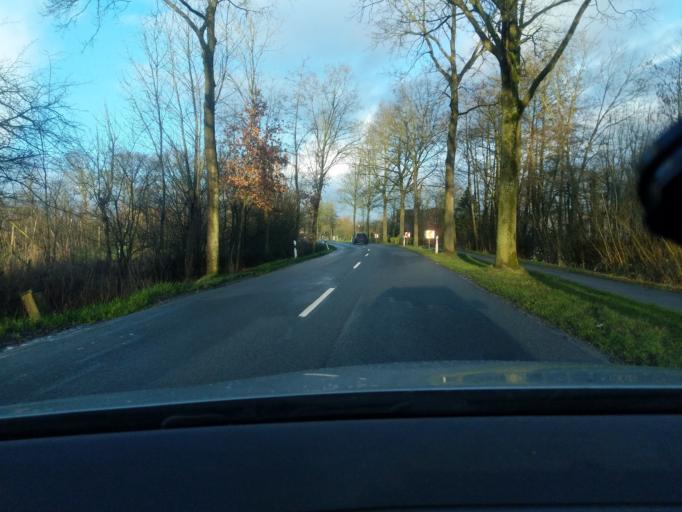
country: DE
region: Lower Saxony
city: Cuxhaven
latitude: 53.8256
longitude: 8.7396
